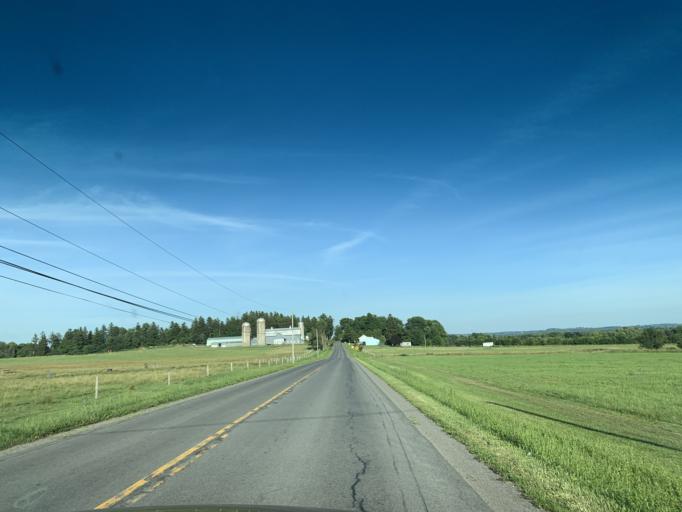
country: US
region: New York
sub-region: Oneida County
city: Clinton
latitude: 43.0528
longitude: -75.4233
